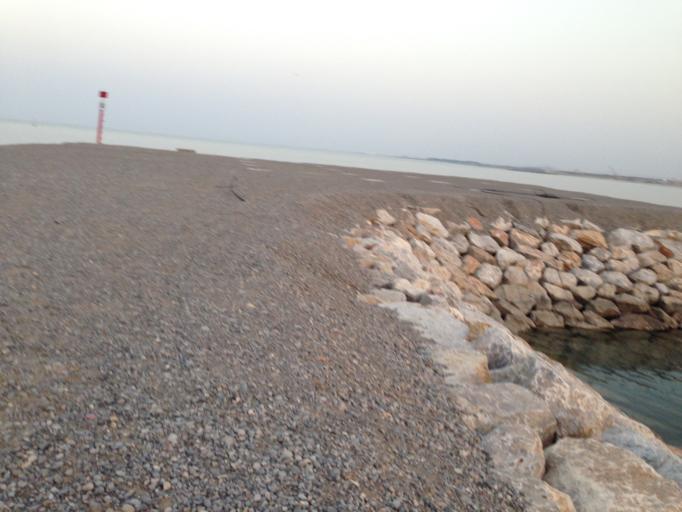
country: OM
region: Muhafazat Masqat
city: As Sib al Jadidah
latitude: 23.6286
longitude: 58.2747
